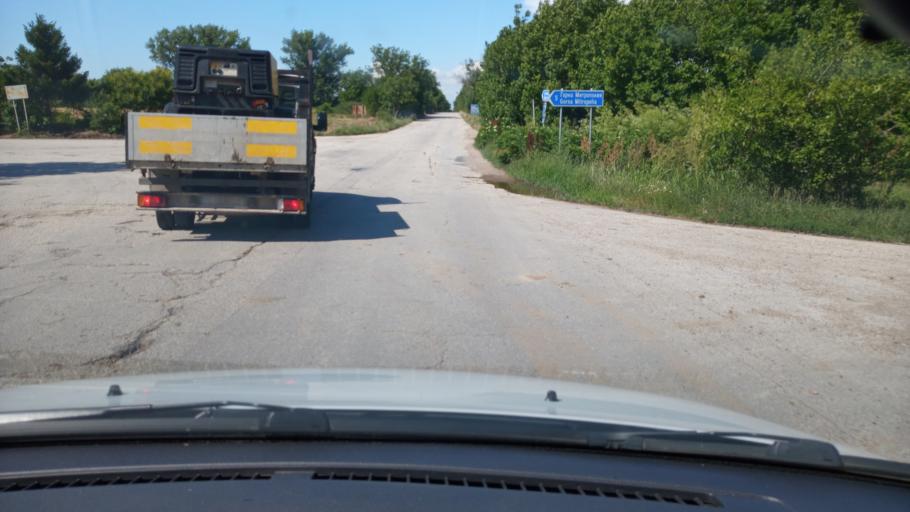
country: BG
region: Pleven
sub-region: Obshtina Dolna Mitropoliya
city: Dolna Mitropoliya
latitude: 43.4418
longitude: 24.5270
